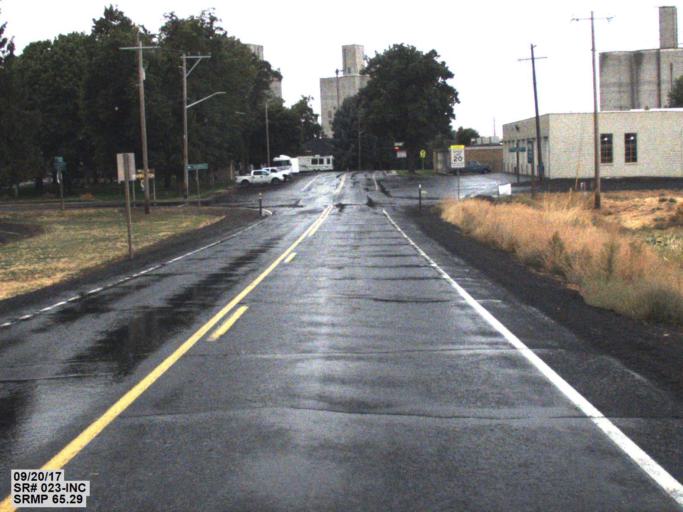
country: US
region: Washington
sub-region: Lincoln County
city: Davenport
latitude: 47.4784
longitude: -118.2497
